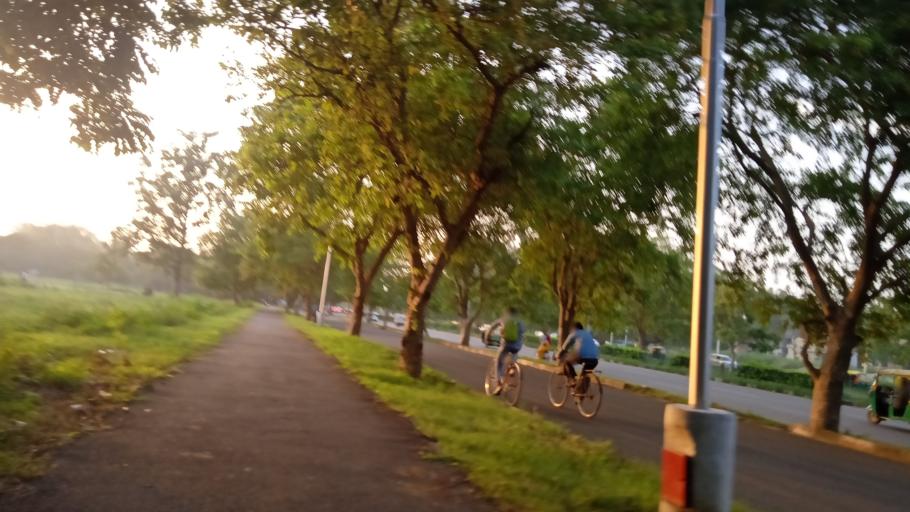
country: IN
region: Chandigarh
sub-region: Chandigarh
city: Chandigarh
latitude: 30.7489
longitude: 76.7506
